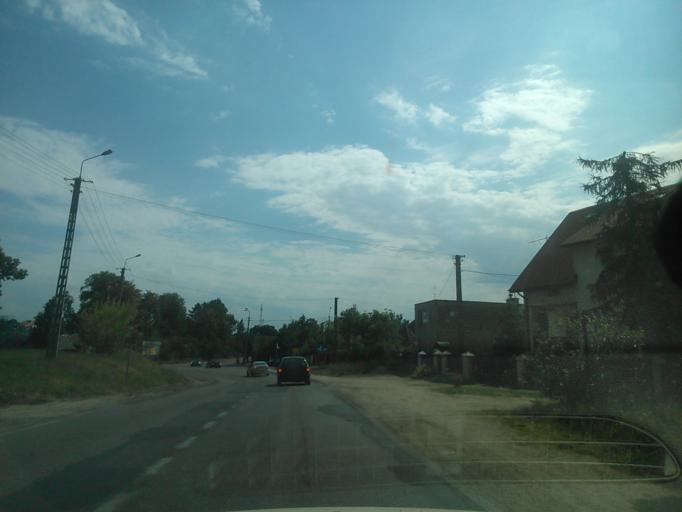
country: PL
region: Masovian Voivodeship
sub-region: Powiat mlawski
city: Mlawa
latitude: 53.1293
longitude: 20.3470
